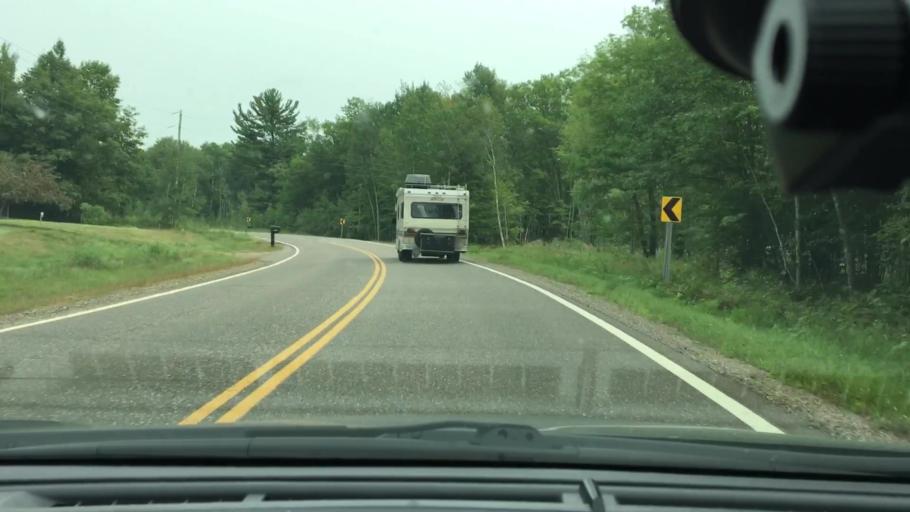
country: US
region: Minnesota
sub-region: Aitkin County
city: Aitkin
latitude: 46.4026
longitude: -93.7949
